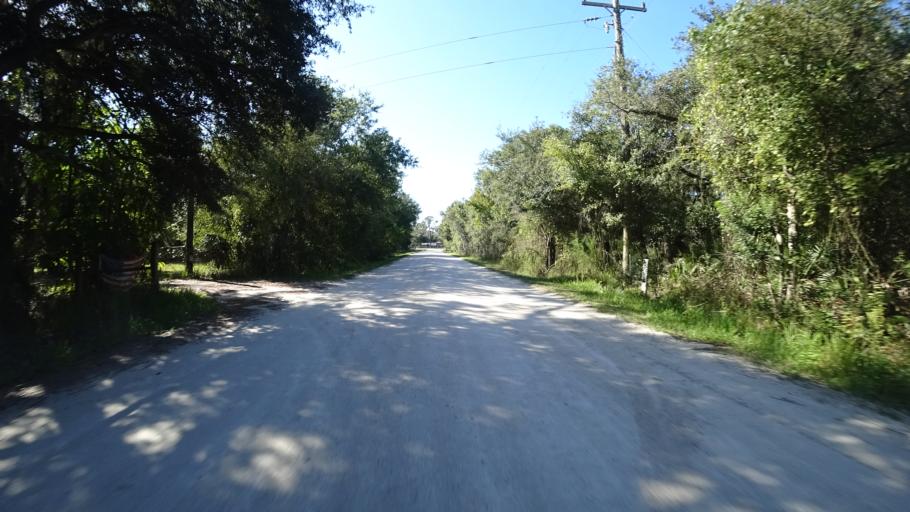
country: US
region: Florida
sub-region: Hillsborough County
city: Sun City Center
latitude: 27.6440
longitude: -82.3533
